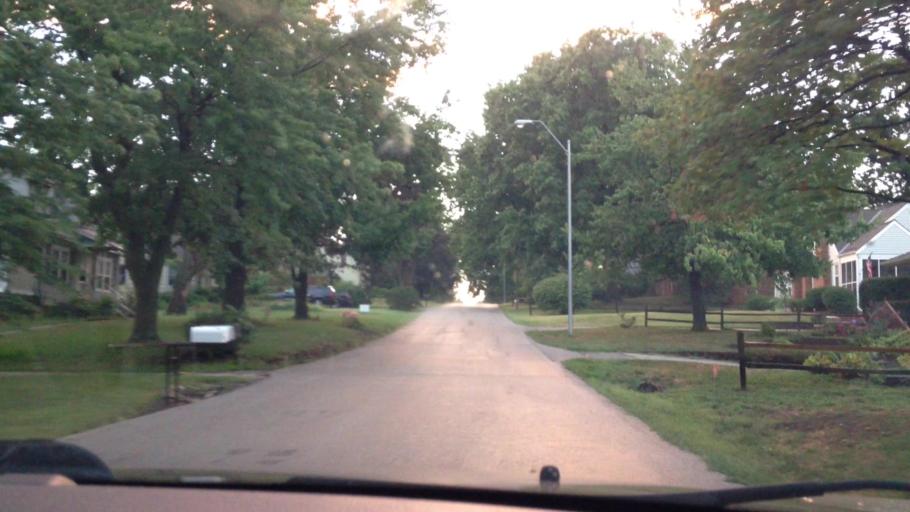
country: US
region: Missouri
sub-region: Clay County
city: Gladstone
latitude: 39.2428
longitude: -94.5780
